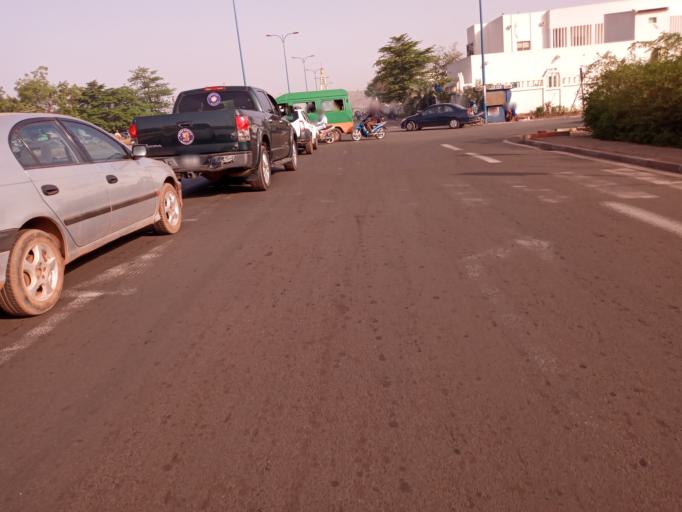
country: ML
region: Bamako
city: Bamako
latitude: 12.6353
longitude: -8.0035
